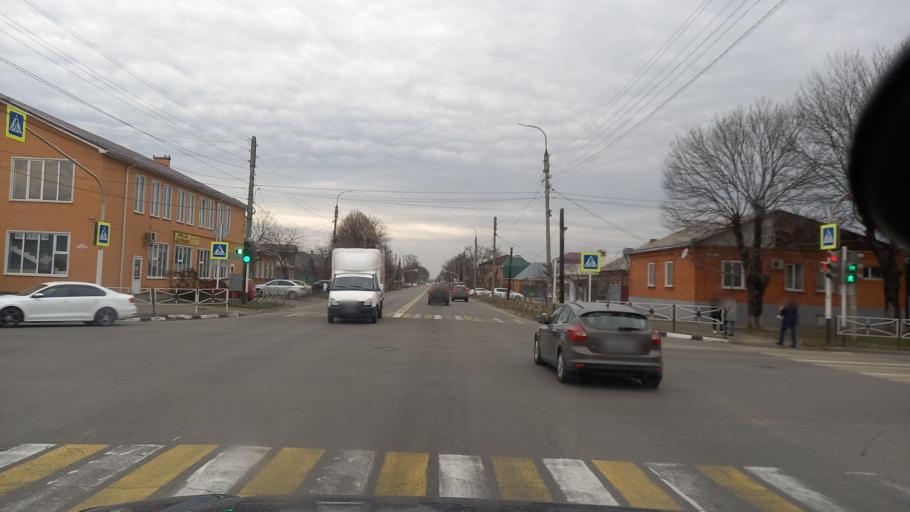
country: RU
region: Adygeya
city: Maykop
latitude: 44.6130
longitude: 40.1015
